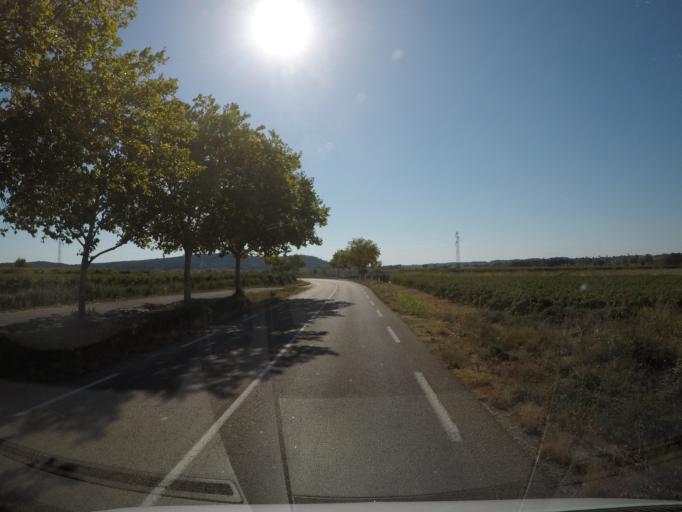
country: FR
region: Languedoc-Roussillon
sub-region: Departement du Gard
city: Ledignan
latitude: 44.0117
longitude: 4.1118
